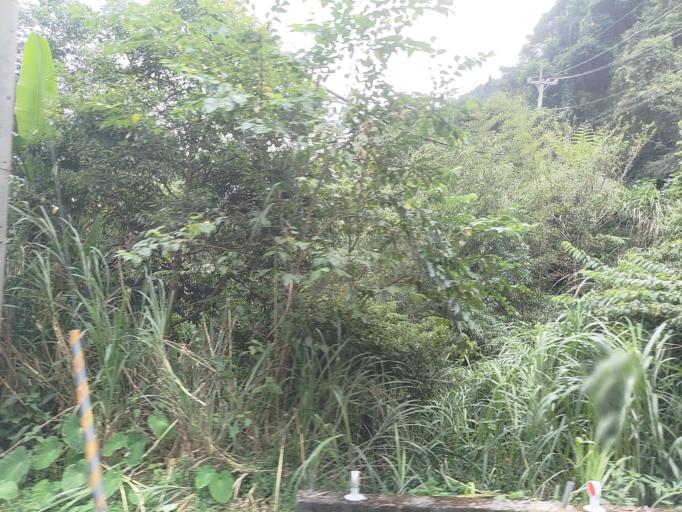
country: TW
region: Taiwan
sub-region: Hsinchu
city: Hsinchu
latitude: 24.6257
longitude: 121.0864
